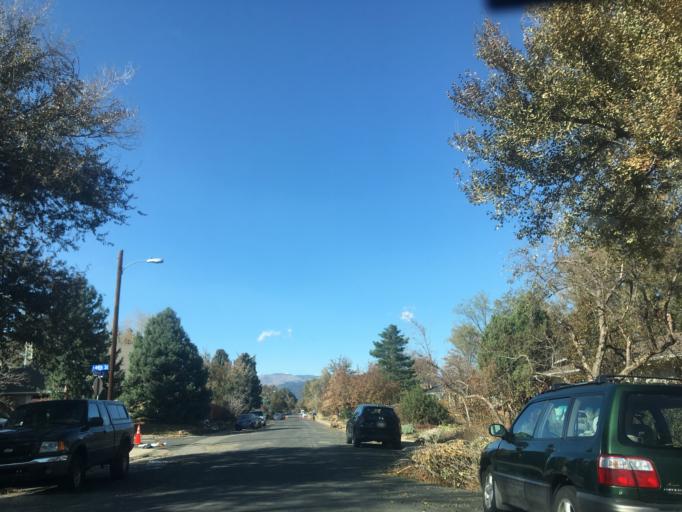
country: US
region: Colorado
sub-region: Boulder County
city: Boulder
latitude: 39.9878
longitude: -105.2427
